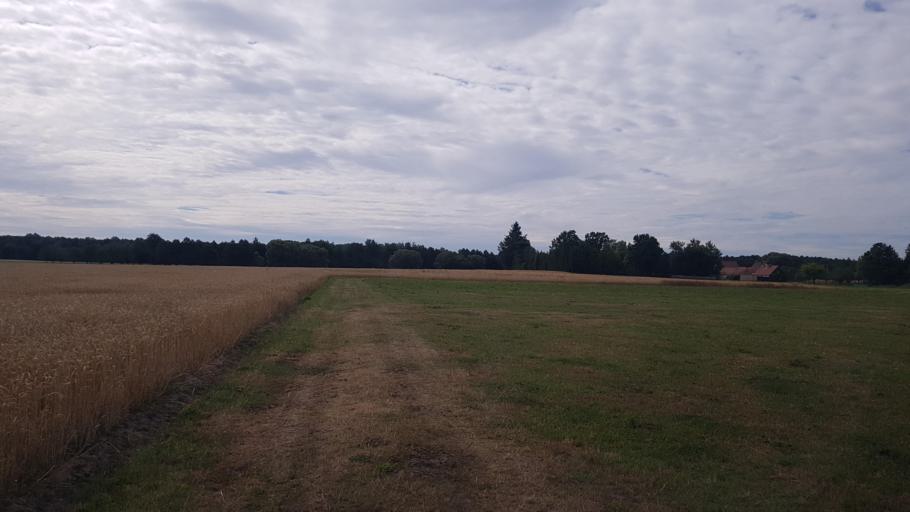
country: DE
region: Brandenburg
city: Finsterwalde
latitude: 51.6270
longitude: 13.7714
